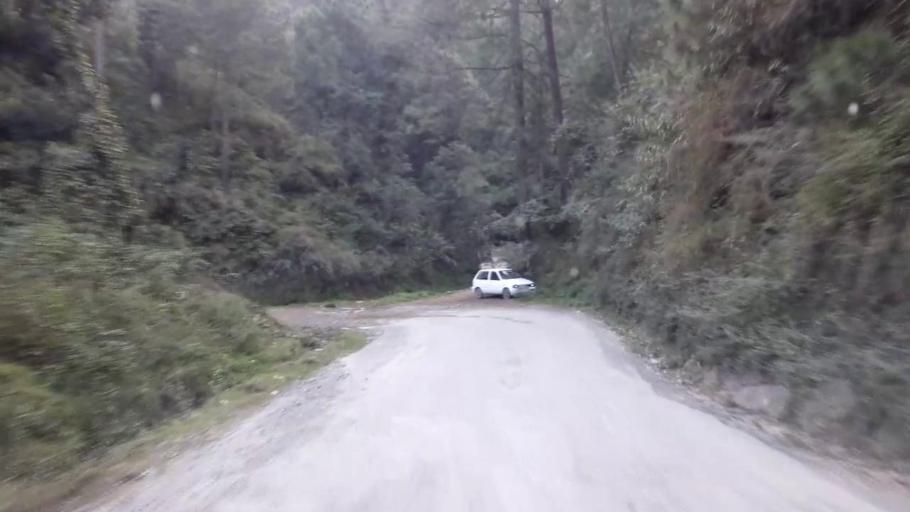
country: IN
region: Himachal Pradesh
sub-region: Shimla
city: Shimla
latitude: 31.0653
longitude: 77.1481
